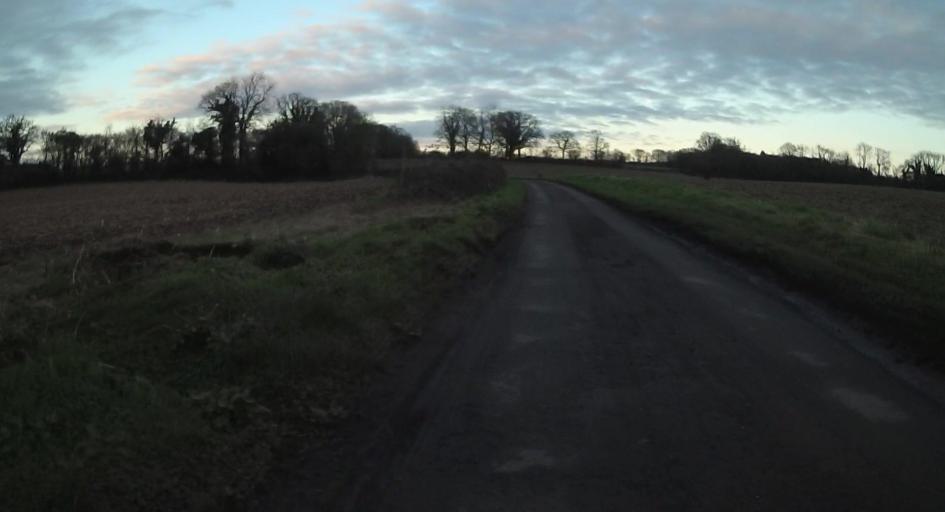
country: GB
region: England
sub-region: Hampshire
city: Swanmore
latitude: 51.0224
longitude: -1.1247
